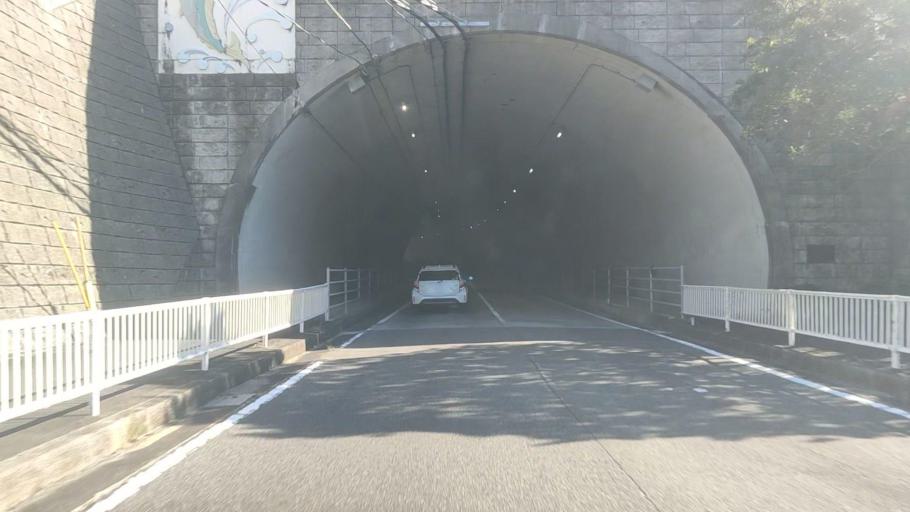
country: JP
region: Oita
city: Saiki
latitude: 32.8011
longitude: 131.9264
